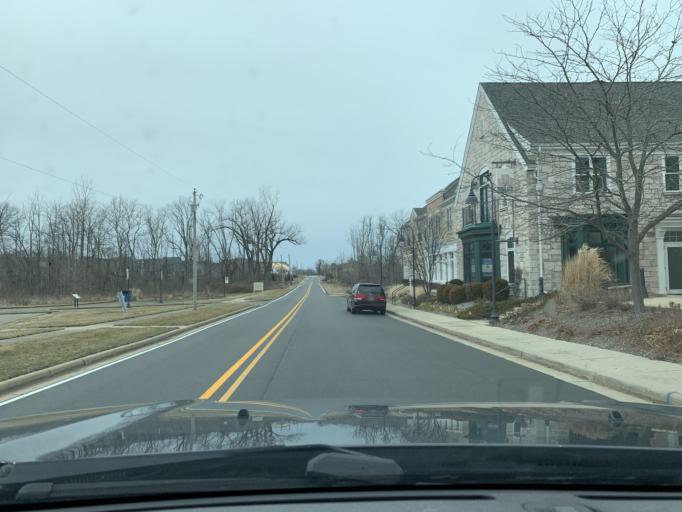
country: US
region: Indiana
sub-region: Porter County
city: Chesterton
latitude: 41.5863
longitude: -87.0357
